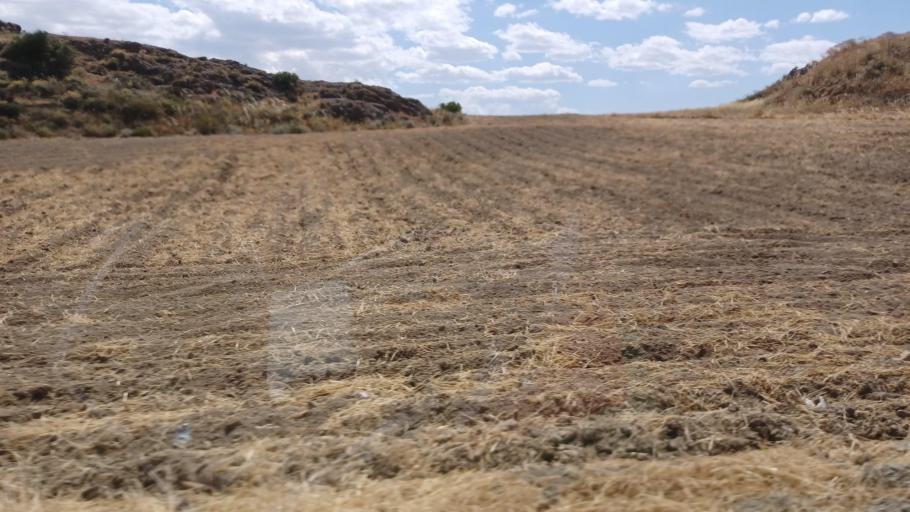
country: CY
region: Larnaka
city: Troulloi
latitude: 35.0061
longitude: 33.5764
